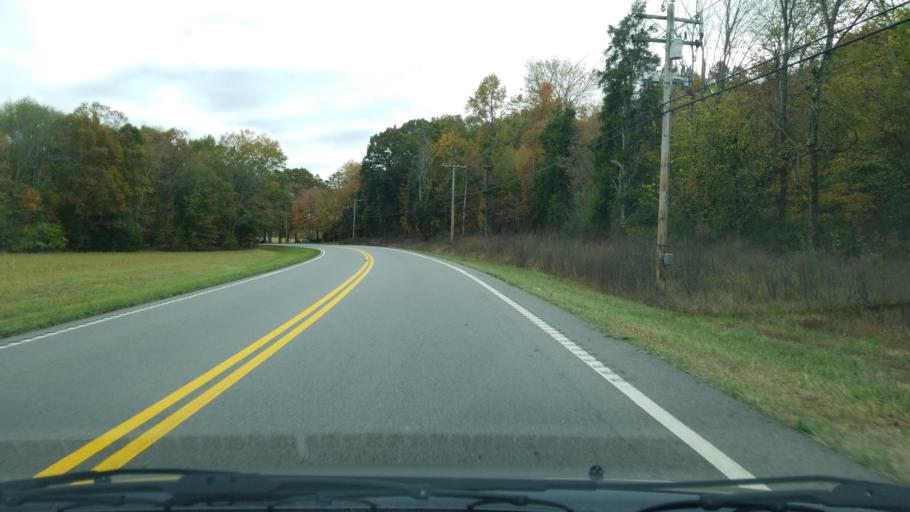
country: US
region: Tennessee
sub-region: Bradley County
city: Hopewell
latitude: 35.3306
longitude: -84.9717
